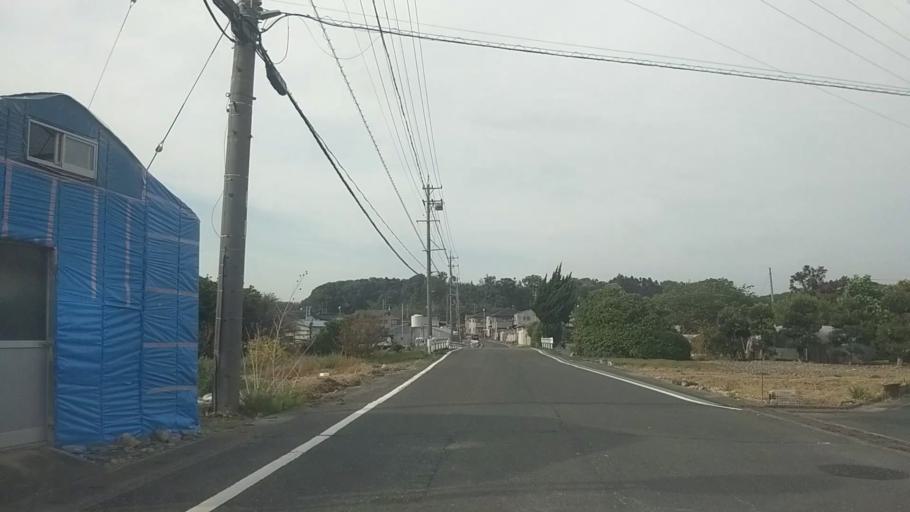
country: JP
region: Shizuoka
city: Kosai-shi
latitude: 34.7418
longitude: 137.6139
